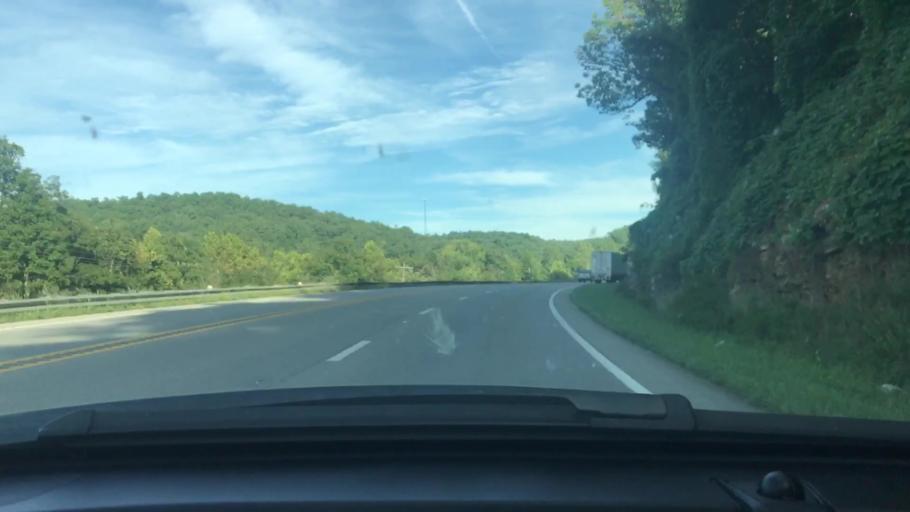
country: US
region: Arkansas
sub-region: Sharp County
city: Cherokee Village
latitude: 36.3039
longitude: -91.4174
